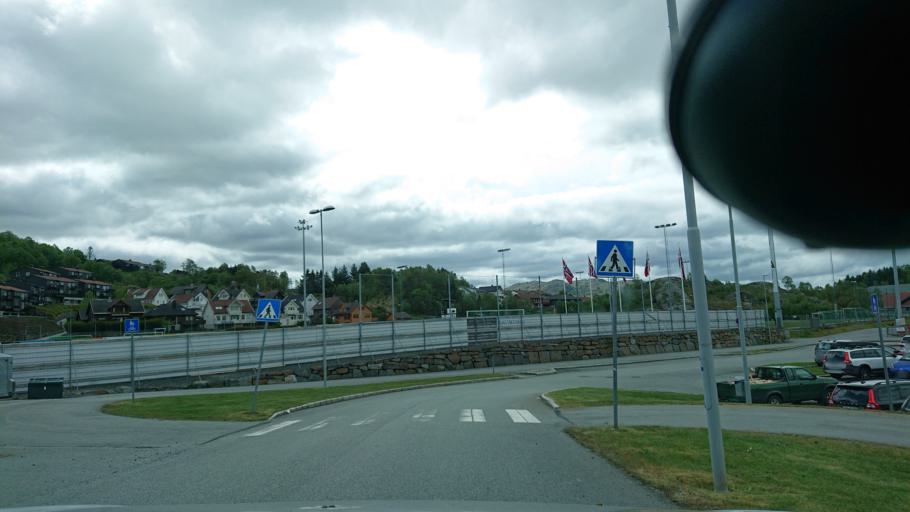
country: NO
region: Rogaland
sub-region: Gjesdal
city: Algard
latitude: 58.7761
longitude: 5.8669
